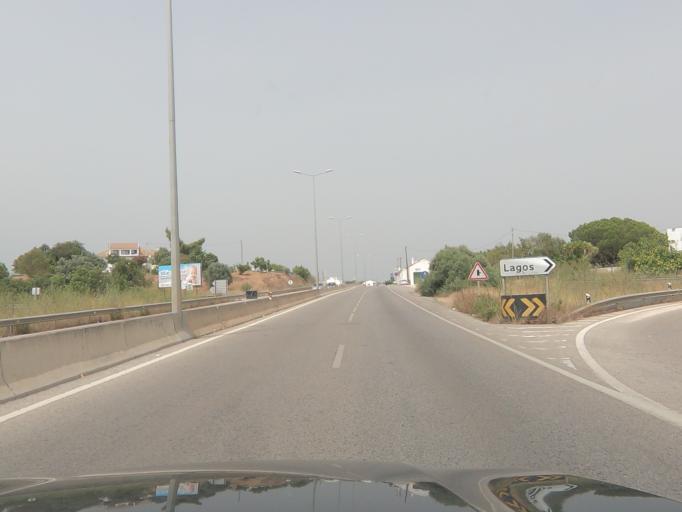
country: PT
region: Faro
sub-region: Portimao
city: Portimao
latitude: 37.1568
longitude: -8.5372
